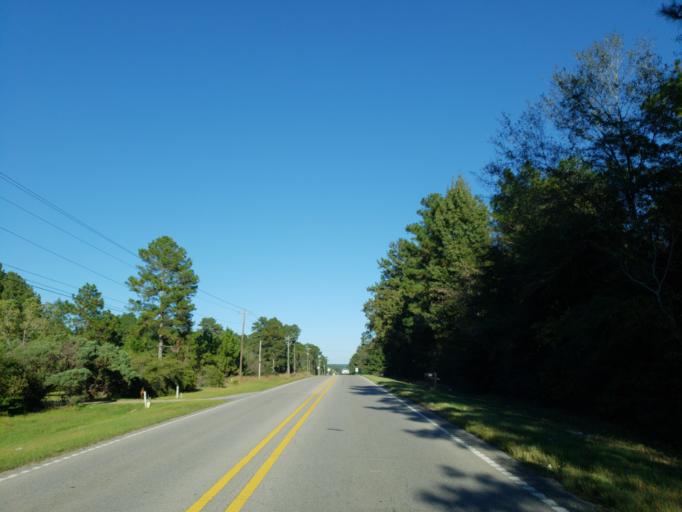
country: US
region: Mississippi
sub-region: Forrest County
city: Petal
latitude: 31.3591
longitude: -89.1559
